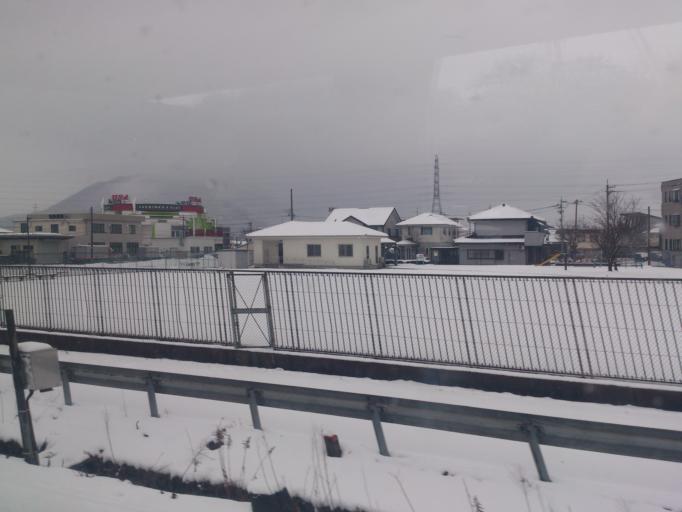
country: JP
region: Fukui
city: Sabae
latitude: 35.9359
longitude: 136.1870
